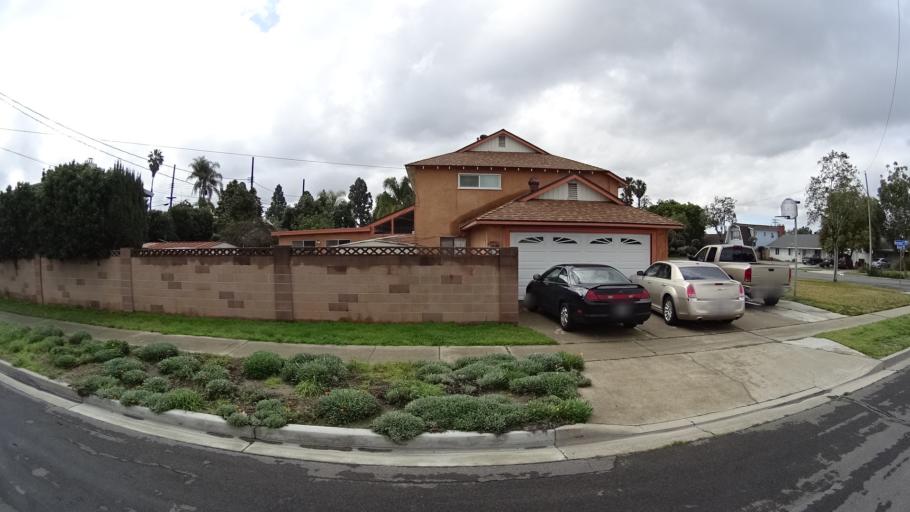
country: US
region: California
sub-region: Orange County
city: Anaheim
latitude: 33.8303
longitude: -117.9450
